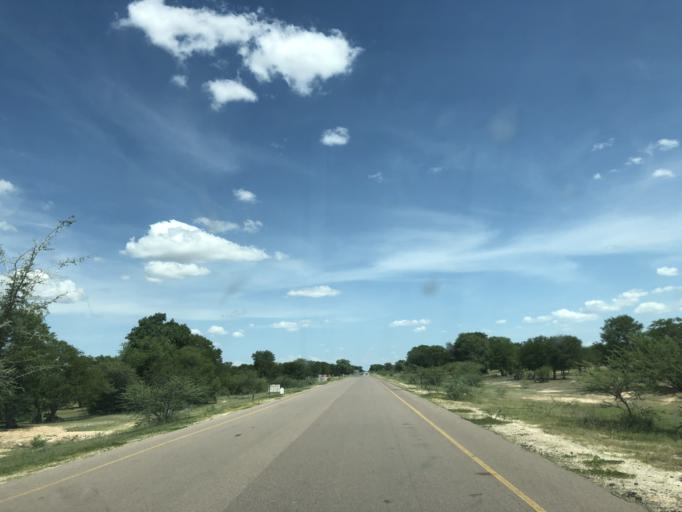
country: AO
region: Cunene
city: Ondjiva
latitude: -16.8436
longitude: 15.4617
